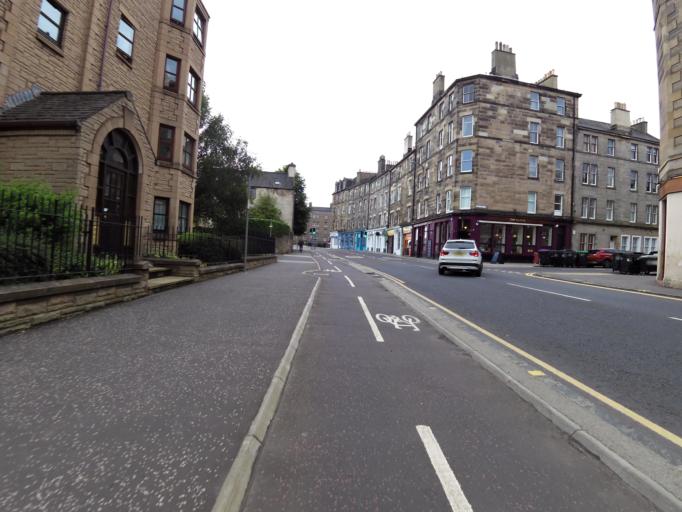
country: GB
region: Scotland
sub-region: Edinburgh
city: Edinburgh
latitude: 55.9425
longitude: -3.1791
